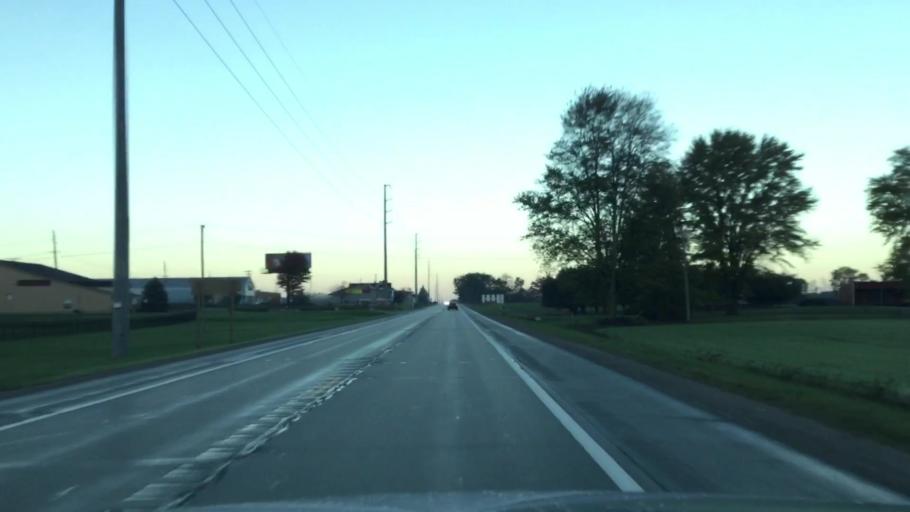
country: US
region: Michigan
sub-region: Livingston County
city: Howell
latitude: 42.6305
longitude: -83.8393
